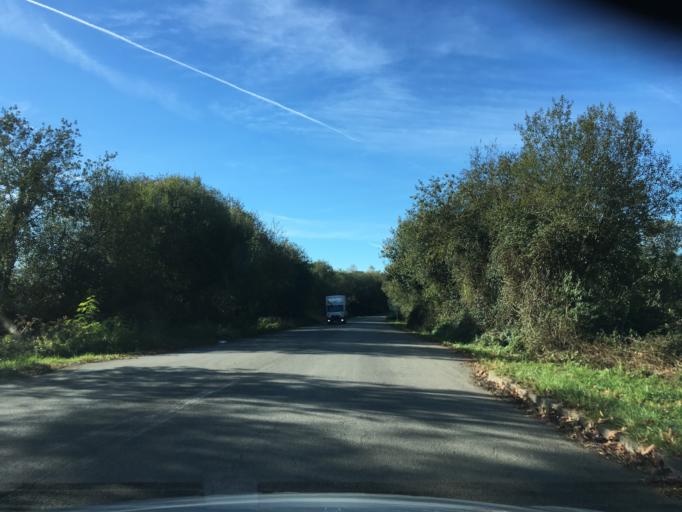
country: FR
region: Aquitaine
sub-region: Departement des Pyrenees-Atlantiques
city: Buros
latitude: 43.3180
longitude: -0.3025
